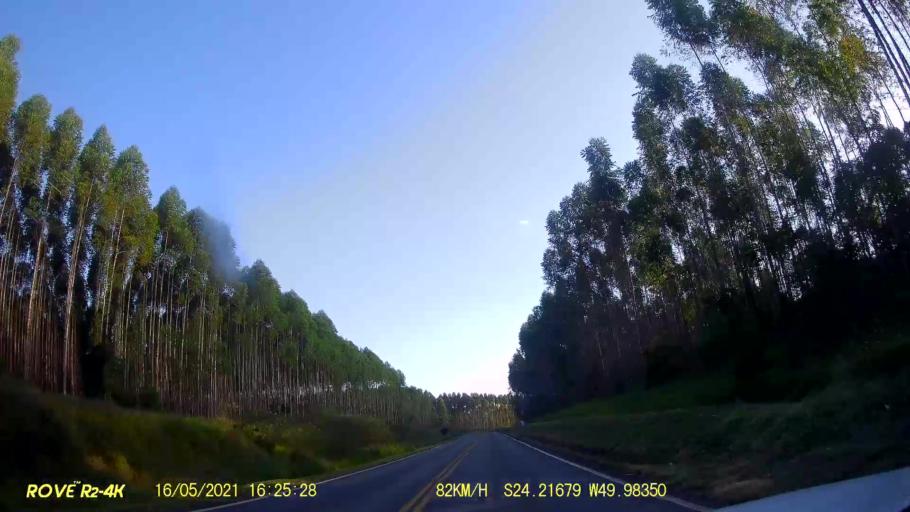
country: BR
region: Parana
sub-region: Jaguariaiva
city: Jaguariaiva
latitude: -24.2171
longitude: -49.9838
